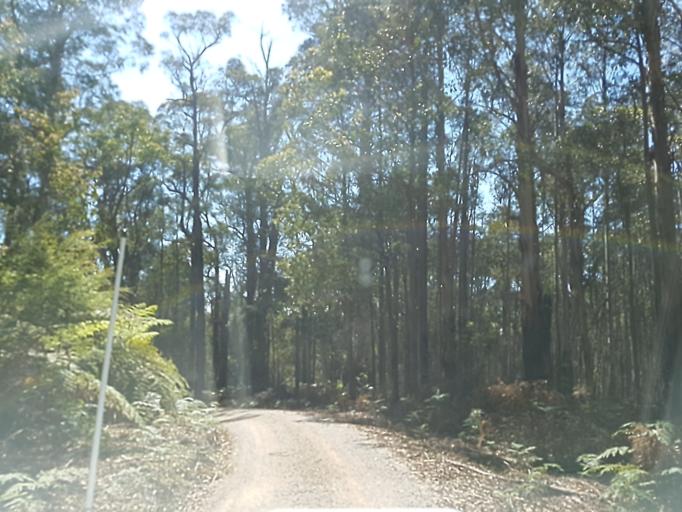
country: AU
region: Victoria
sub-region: East Gippsland
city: Lakes Entrance
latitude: -37.2916
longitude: 148.3197
